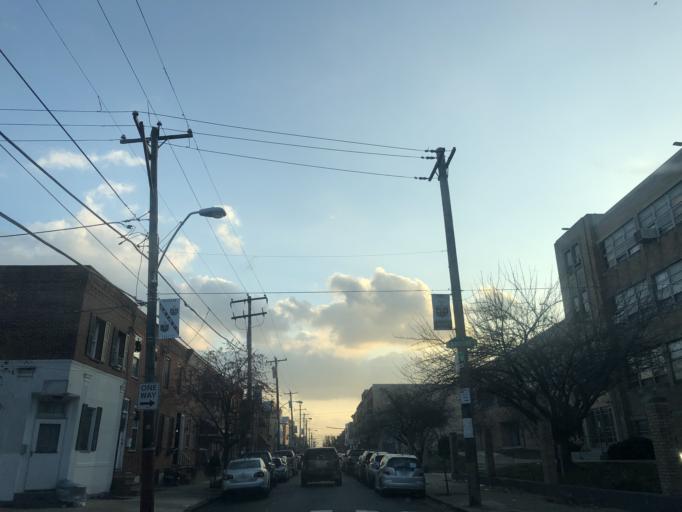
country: US
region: Pennsylvania
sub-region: Philadelphia County
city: Philadelphia
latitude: 39.9273
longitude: -75.1621
